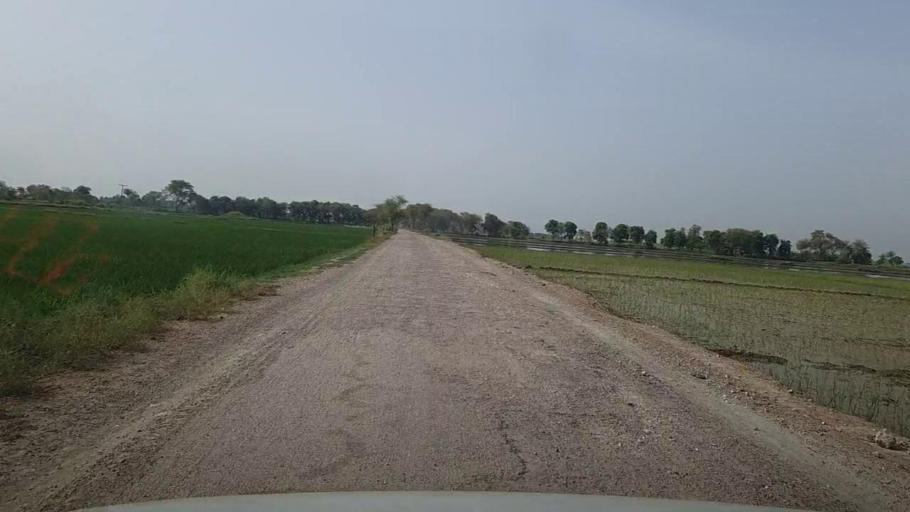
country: PK
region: Sindh
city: Mehar
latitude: 27.1067
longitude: 67.8207
